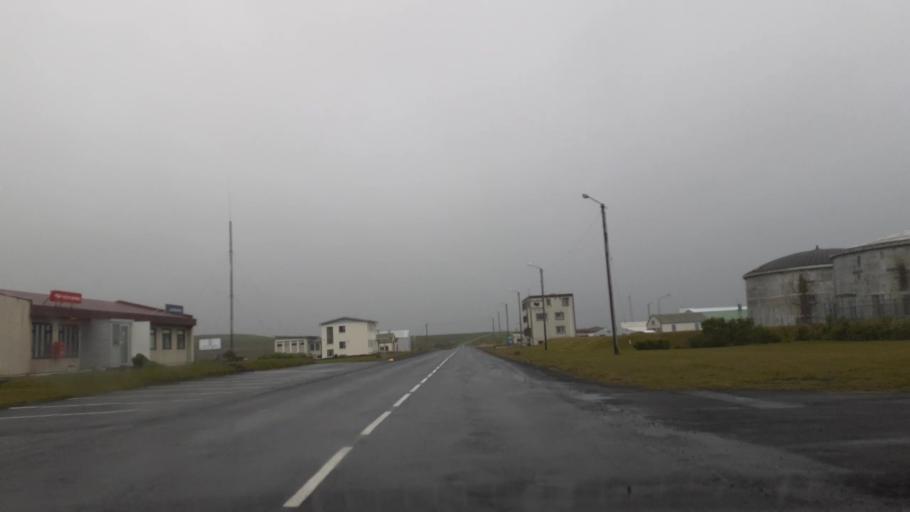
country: IS
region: Northeast
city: Husavik
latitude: 66.4542
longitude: -15.9506
